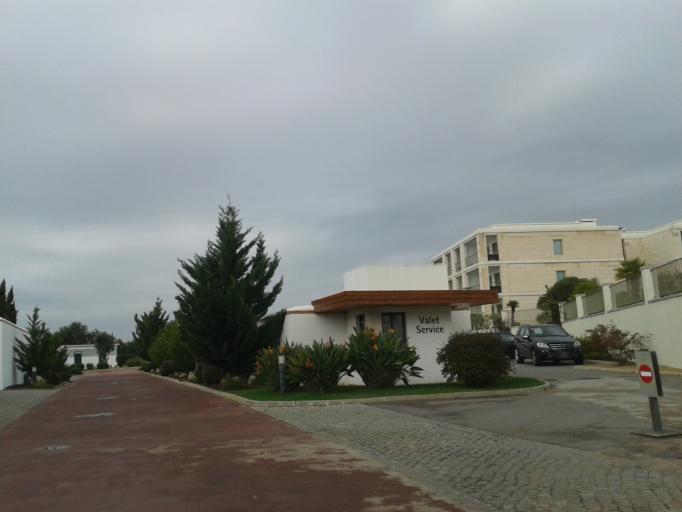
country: PT
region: Faro
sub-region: Loule
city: Boliqueime
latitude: 37.1028
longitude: -8.1430
